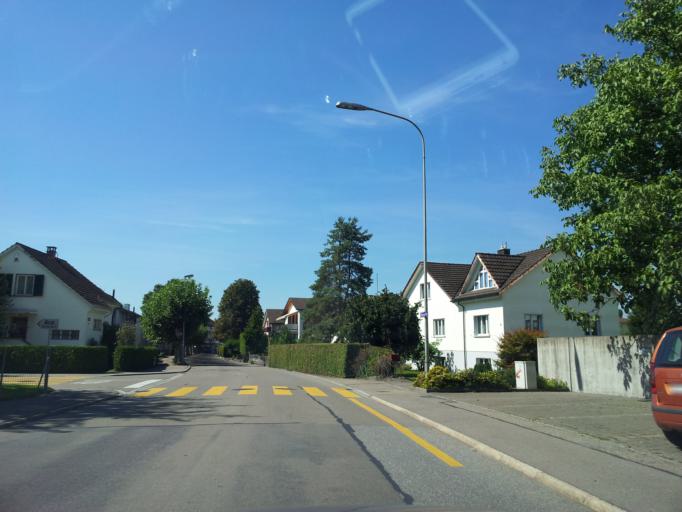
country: CH
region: Saint Gallen
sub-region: Wahlkreis See-Gaster
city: Rapperswil
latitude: 47.2225
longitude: 8.8317
